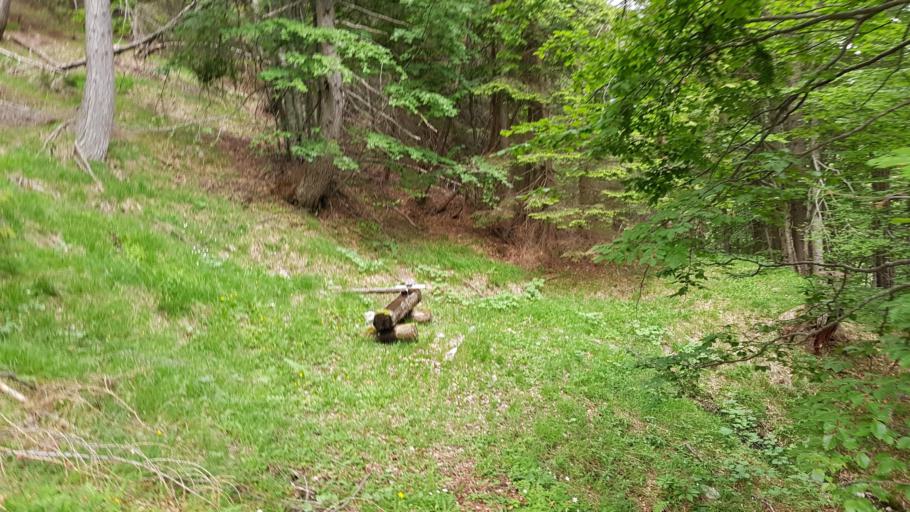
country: IT
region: Friuli Venezia Giulia
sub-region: Provincia di Udine
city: Pontebba
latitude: 46.5350
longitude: 13.2819
